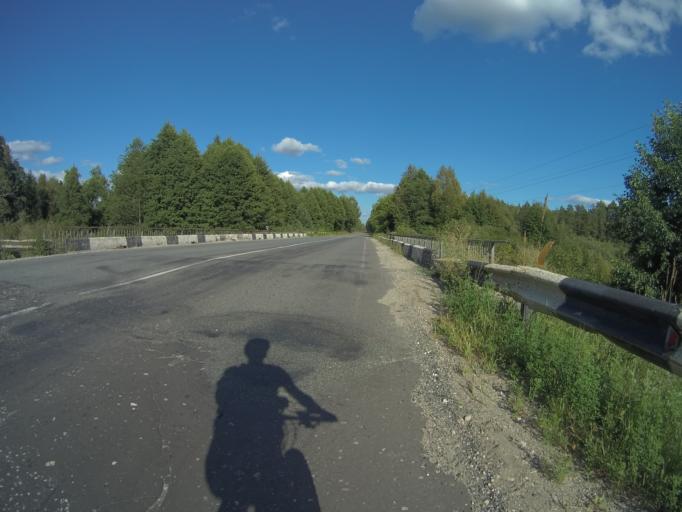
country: RU
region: Vladimir
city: Mezinovskiy
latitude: 55.5952
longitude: 40.3809
